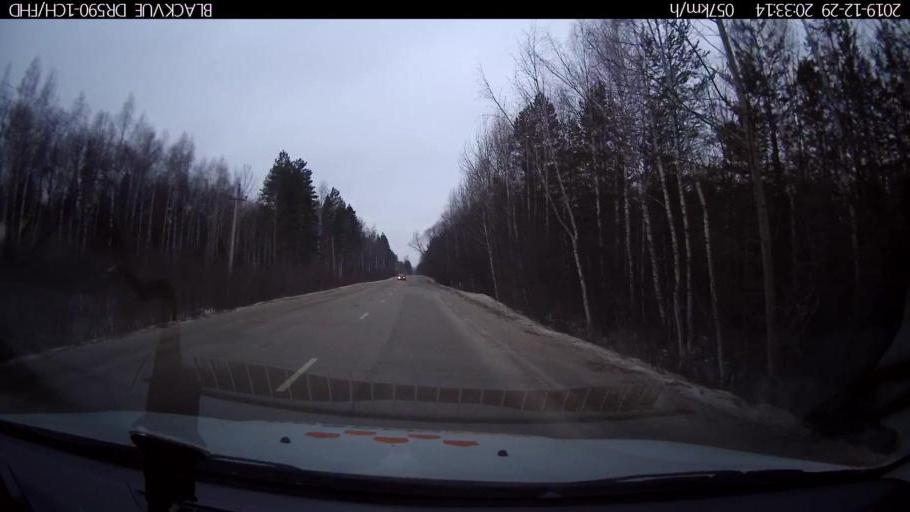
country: RU
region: Nizjnij Novgorod
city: Afonino
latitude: 56.1794
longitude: 44.0543
